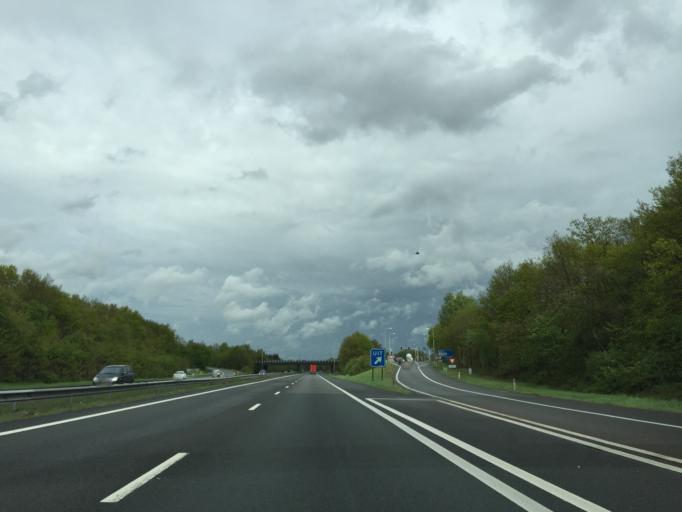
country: NL
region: Gelderland
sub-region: Gemeente Harderwijk
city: Harderwijk
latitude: 52.3352
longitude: 5.6411
